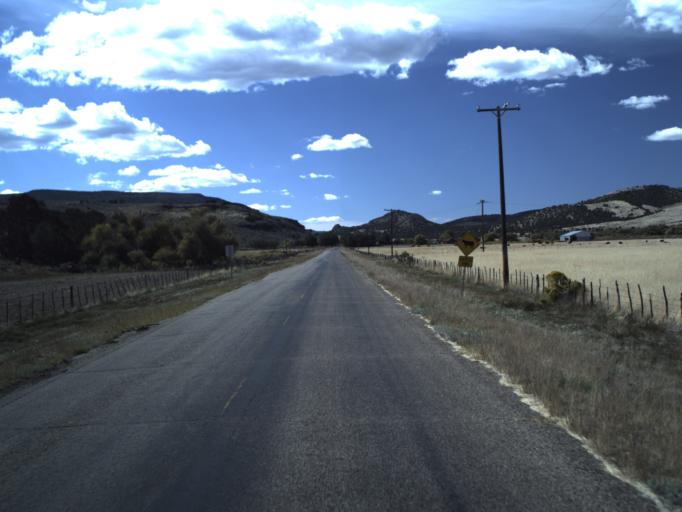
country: US
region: Utah
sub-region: Washington County
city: Enterprise
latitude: 37.5735
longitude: -113.7359
